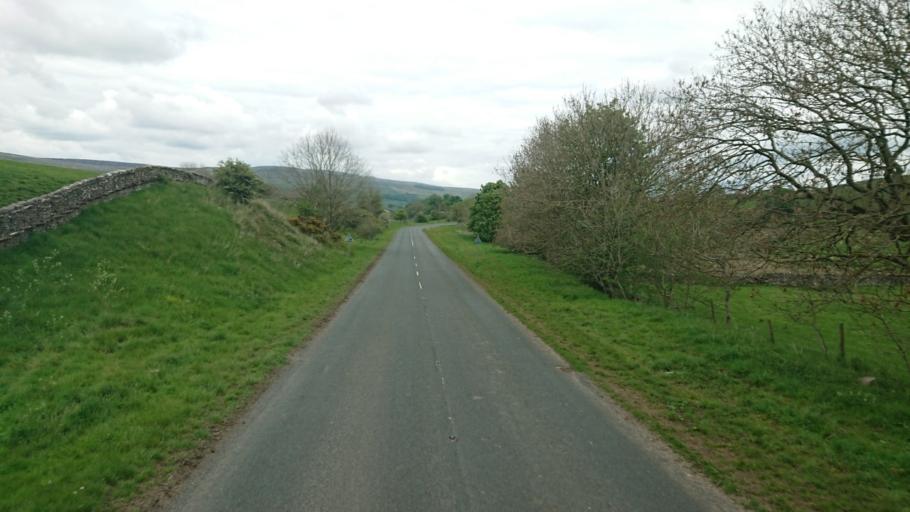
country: GB
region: England
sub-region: County Durham
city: Bowes
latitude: 54.3070
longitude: -2.1207
